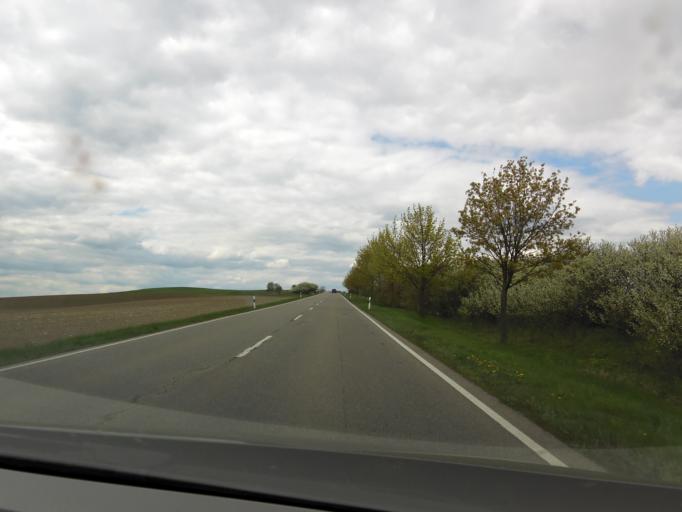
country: DE
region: Saxony-Anhalt
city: Eckartsberga
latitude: 51.1163
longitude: 11.5944
